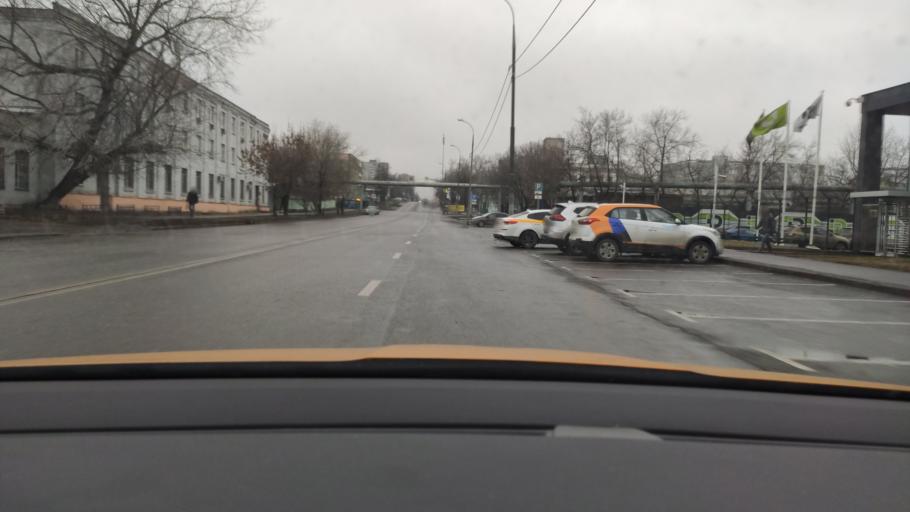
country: RU
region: Moscow
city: Lefortovo
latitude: 55.7365
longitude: 37.7205
